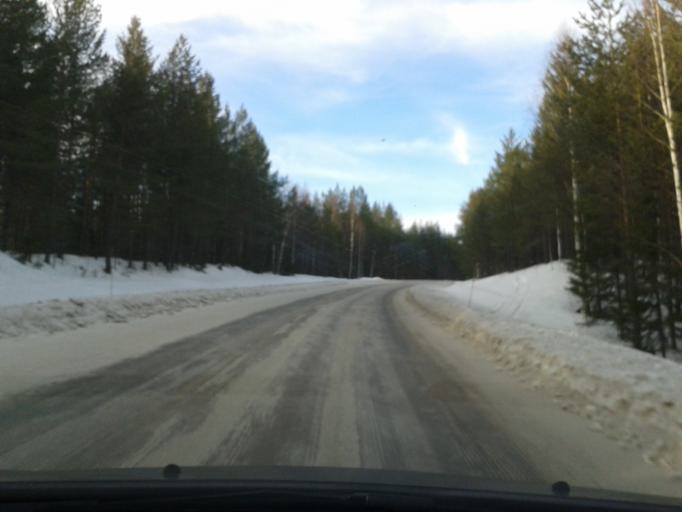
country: SE
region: Vaesternorrland
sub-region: OErnskoeldsviks Kommun
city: Bredbyn
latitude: 63.5315
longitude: 17.9694
